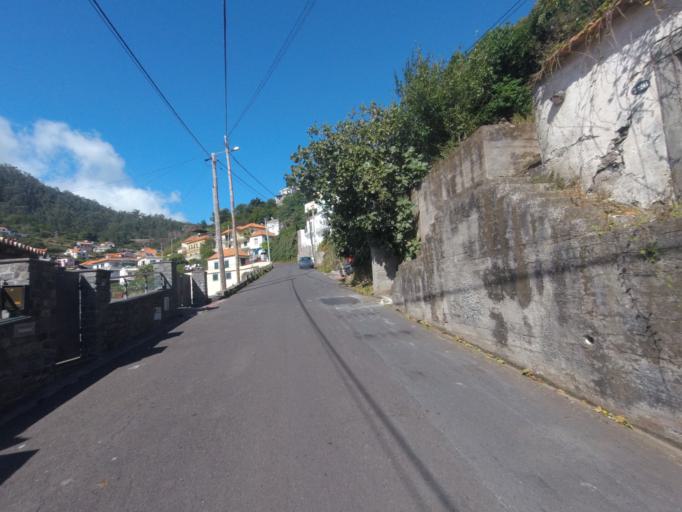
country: PT
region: Madeira
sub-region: Ribeira Brava
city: Campanario
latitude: 32.6771
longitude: -17.0300
